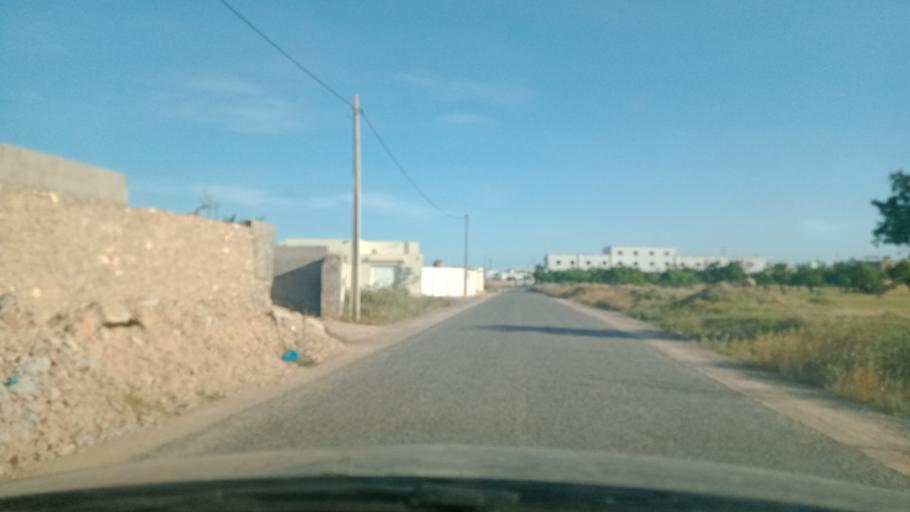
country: TN
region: Safaqis
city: Sfax
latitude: 34.8169
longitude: 10.7360
